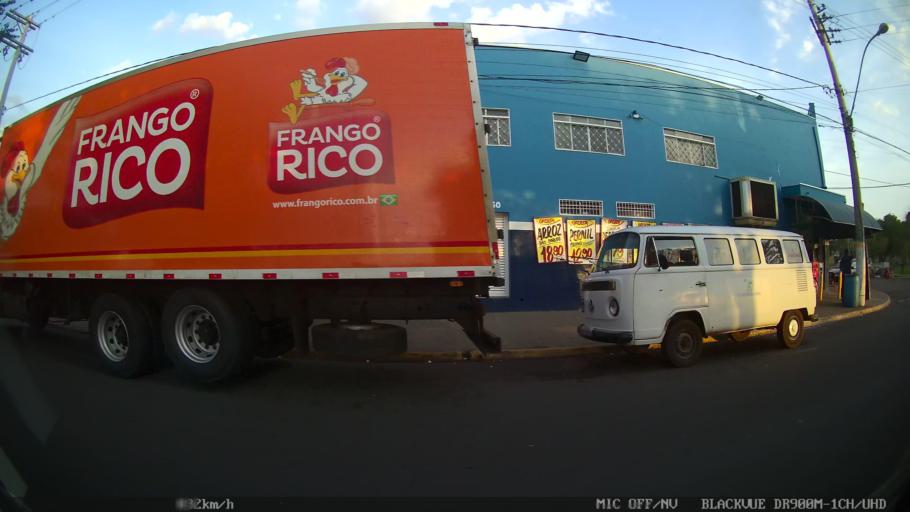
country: BR
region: Sao Paulo
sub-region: Ribeirao Preto
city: Ribeirao Preto
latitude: -21.1258
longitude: -47.8265
